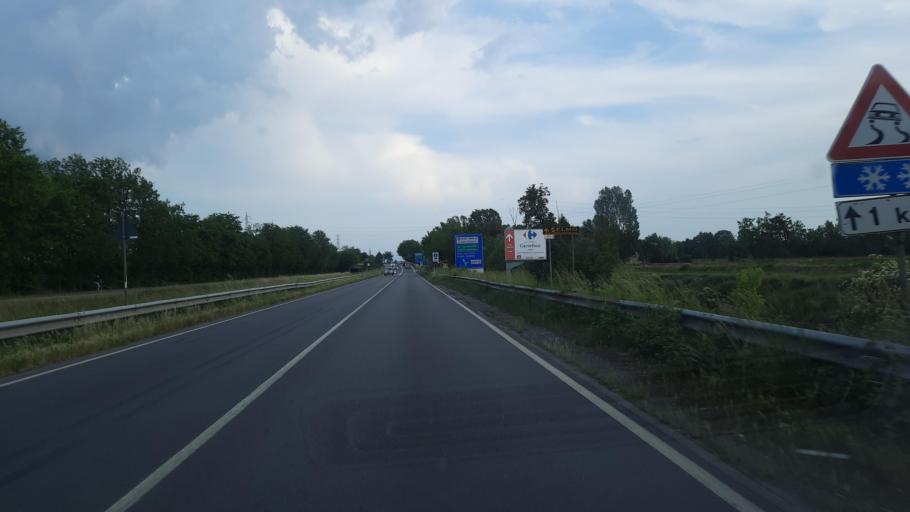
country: IT
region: Lombardy
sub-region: Provincia di Pavia
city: Borgarello
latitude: 45.2175
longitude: 9.1439
